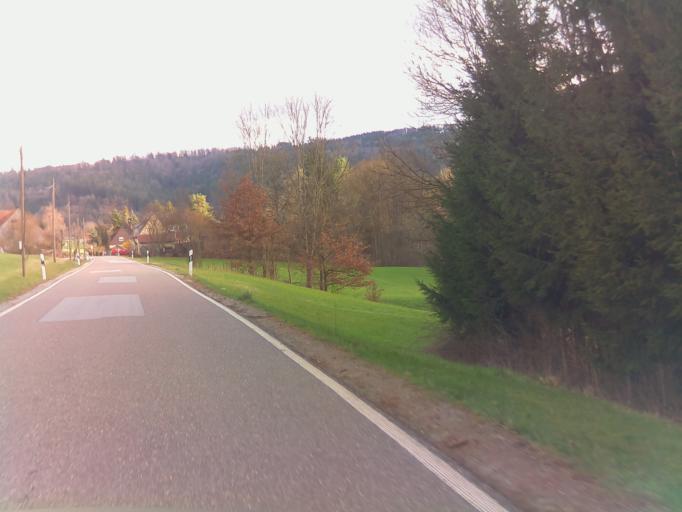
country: DE
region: Baden-Wuerttemberg
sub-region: Regierungsbezirk Stuttgart
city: Lorch
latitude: 48.8056
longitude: 9.6601
